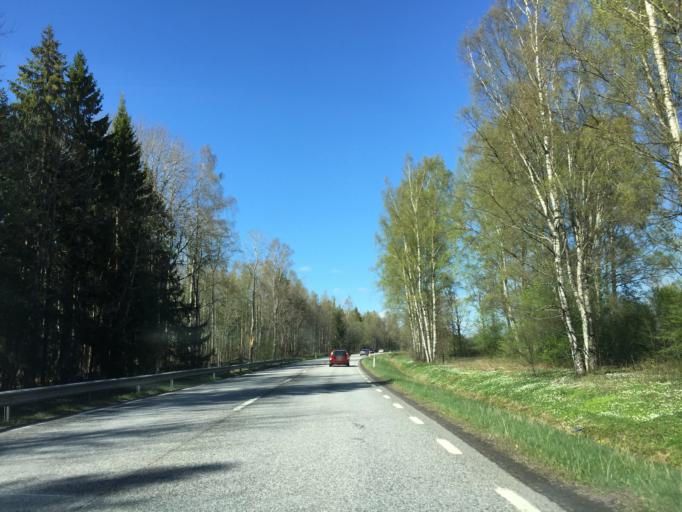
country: SE
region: OErebro
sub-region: Hallsbergs Kommun
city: Skollersta
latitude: 59.1450
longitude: 15.2704
